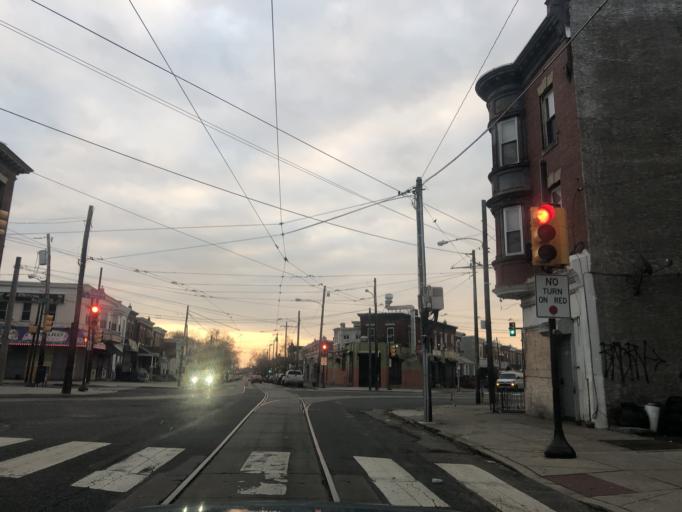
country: US
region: Pennsylvania
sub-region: Delaware County
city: Millbourne
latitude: 39.9699
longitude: -75.2397
